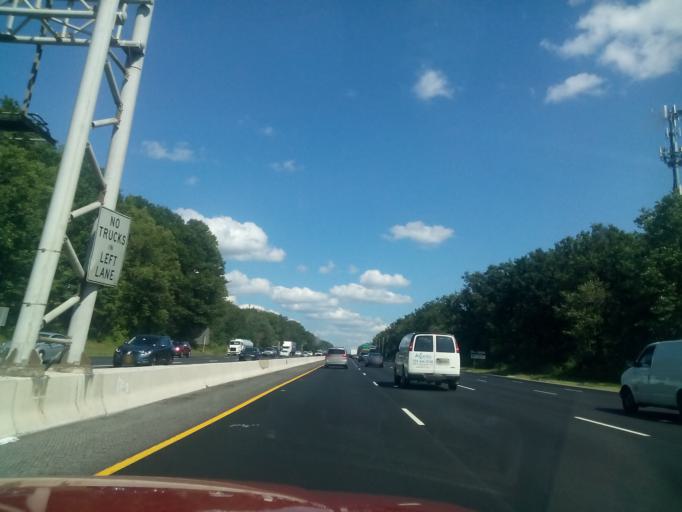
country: US
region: New Jersey
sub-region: Morris County
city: Dover
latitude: 40.9104
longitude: -74.5576
